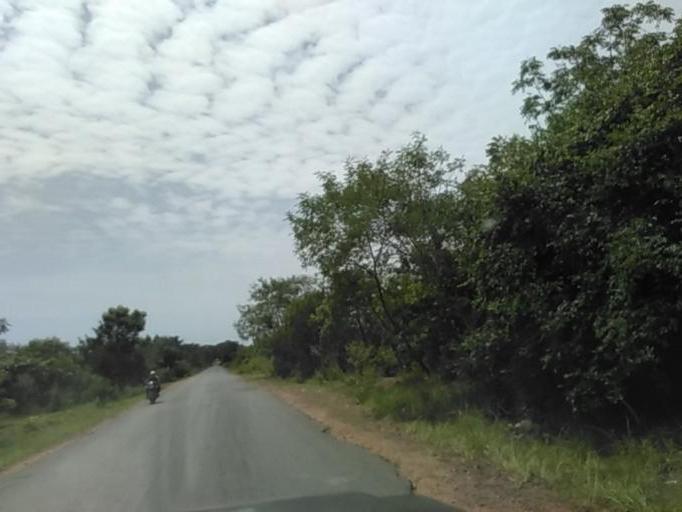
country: GH
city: Akropong
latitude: 6.0929
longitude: 0.0719
